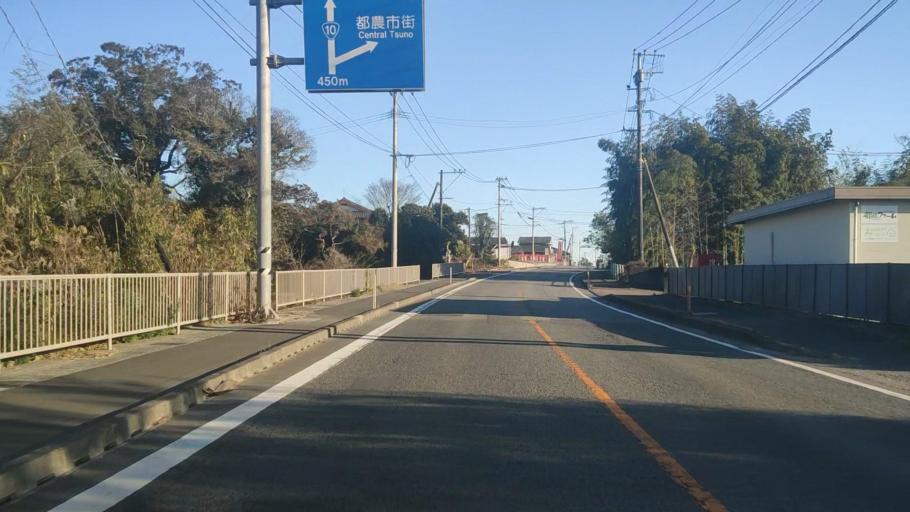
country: JP
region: Miyazaki
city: Takanabe
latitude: 32.2416
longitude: 131.5492
